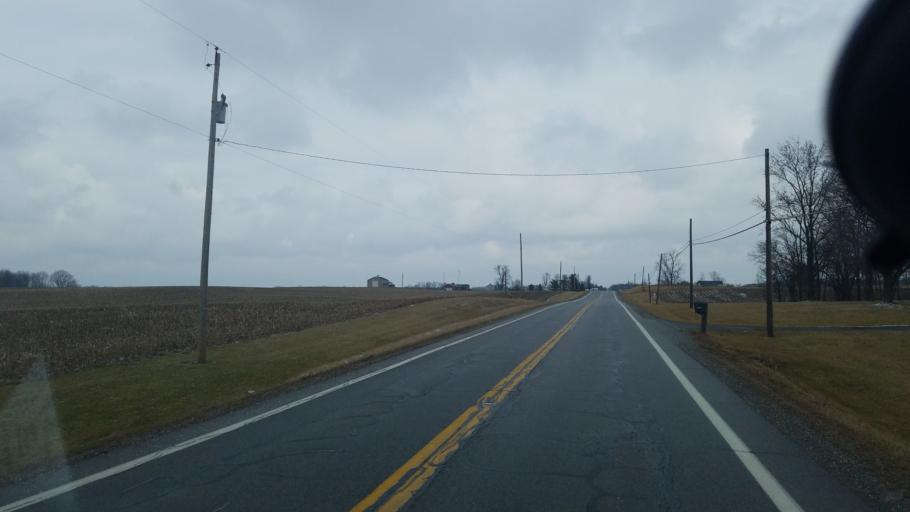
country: US
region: Ohio
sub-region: Morrow County
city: Mount Gilead
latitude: 40.5954
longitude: -82.8237
